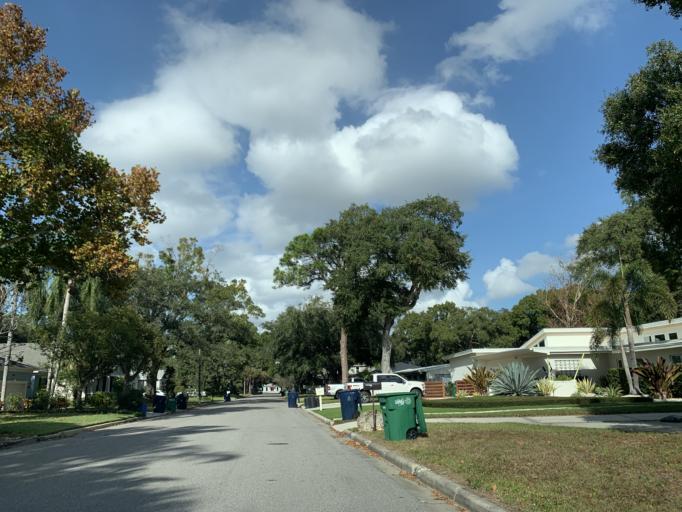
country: US
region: Florida
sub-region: Hillsborough County
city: Tampa
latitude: 27.9091
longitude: -82.5153
